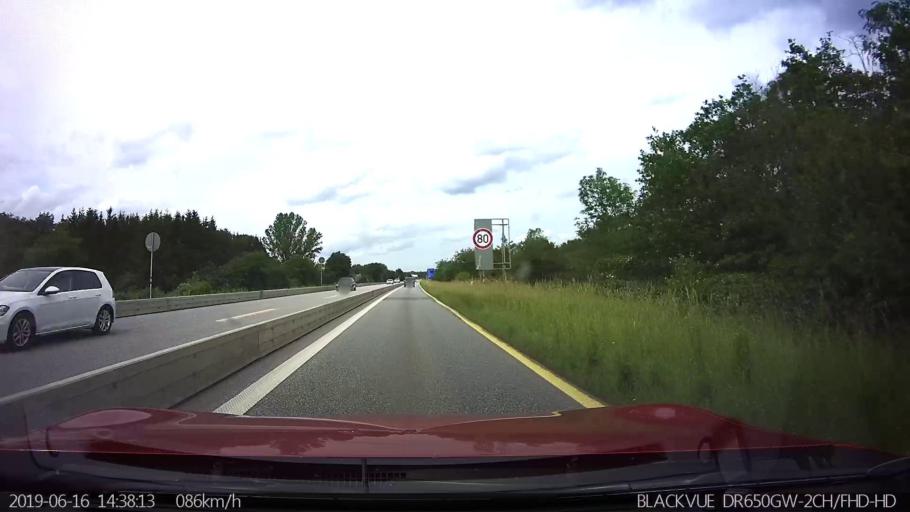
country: DE
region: Schleswig-Holstein
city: Mielkendorf
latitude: 54.2916
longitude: 10.0477
